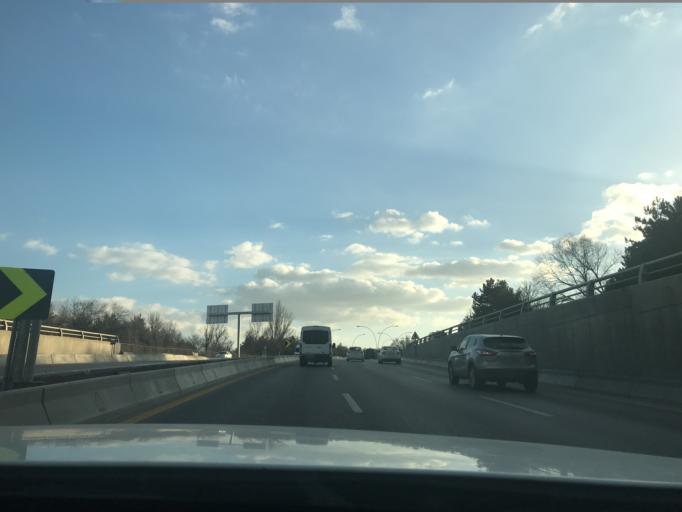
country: TR
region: Ankara
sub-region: Goelbasi
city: Golbasi
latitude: 39.8478
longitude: 32.8106
